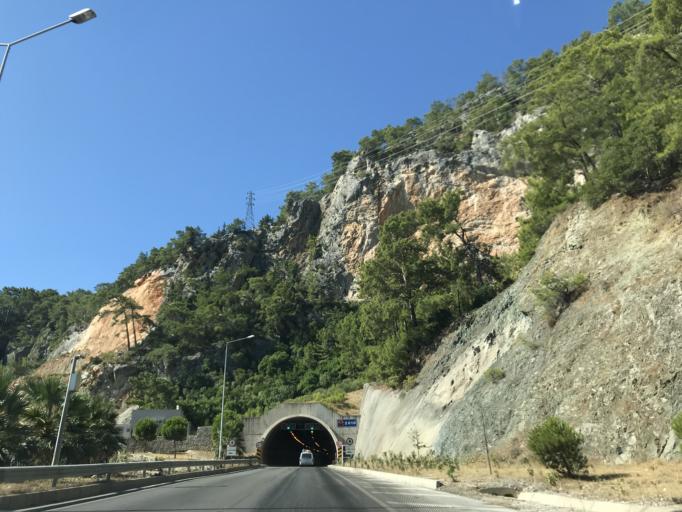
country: TR
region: Antalya
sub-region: Kemer
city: Goeynuek
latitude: 36.7513
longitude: 30.5667
